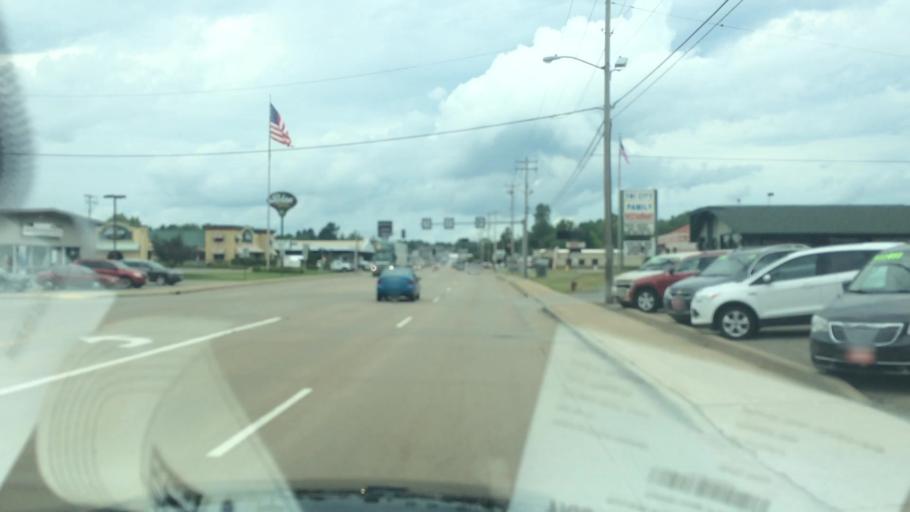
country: US
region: Wisconsin
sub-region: Marathon County
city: Schofield
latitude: 44.9242
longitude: -89.6132
